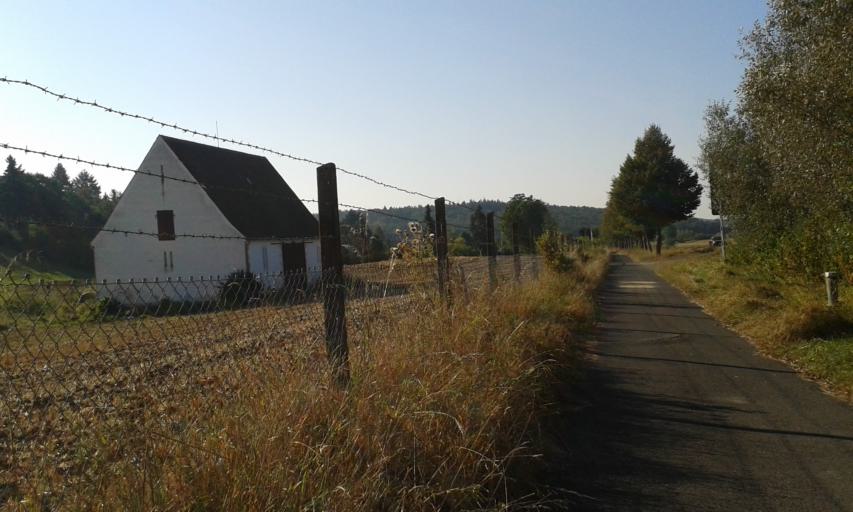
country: DE
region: Bavaria
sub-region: Upper Franconia
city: Bamberg
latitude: 49.8693
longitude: 10.8832
